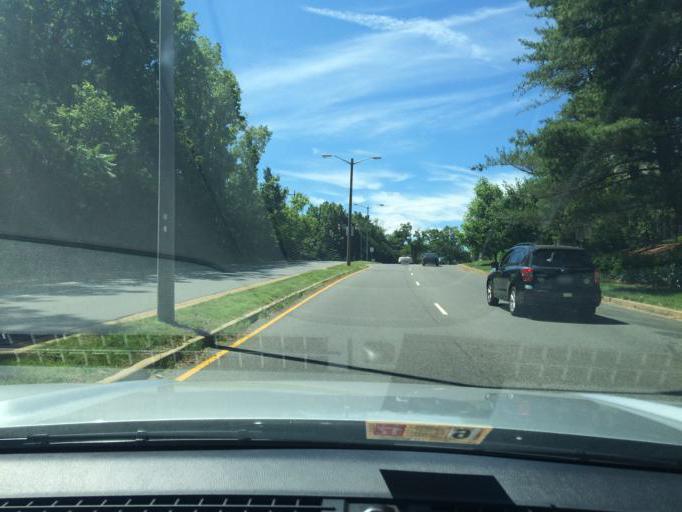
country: US
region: Virginia
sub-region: Fairfax County
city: Baileys Crossroads
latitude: 38.8373
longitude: -77.0847
